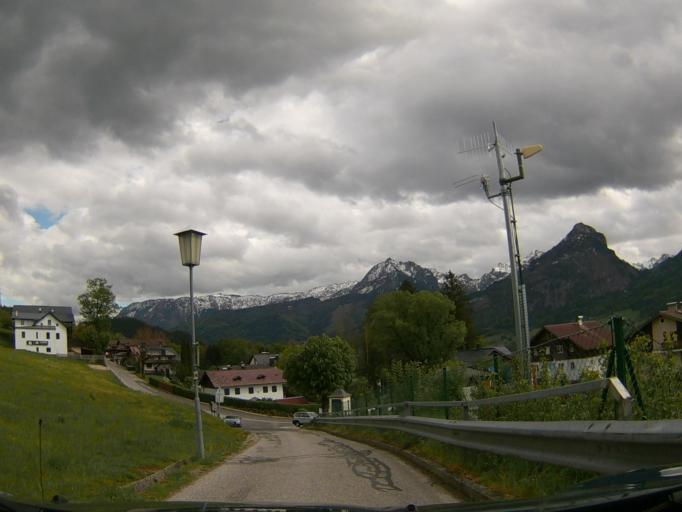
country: AT
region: Upper Austria
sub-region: Politischer Bezirk Gmunden
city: Sankt Wolfgang im Salzkammergut
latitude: 47.7374
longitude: 13.4524
